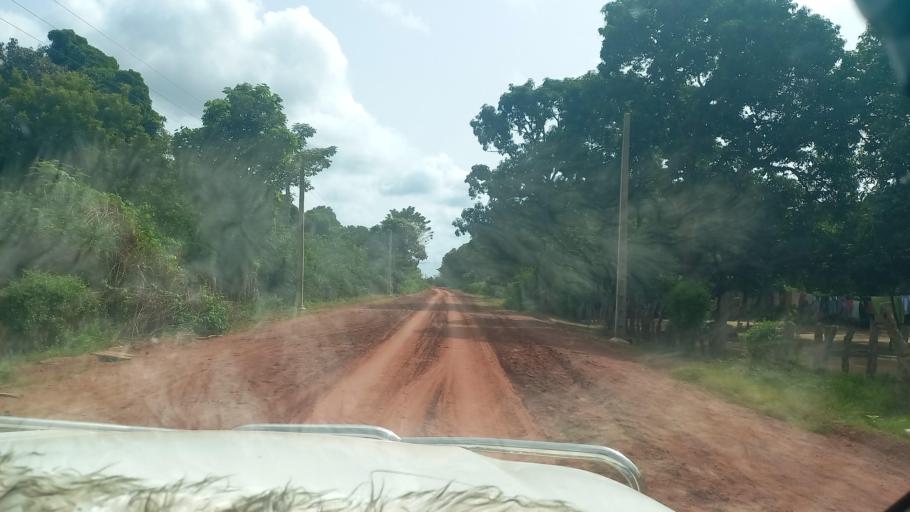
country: SN
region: Ziguinchor
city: Bignona
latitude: 12.7567
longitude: -16.2680
